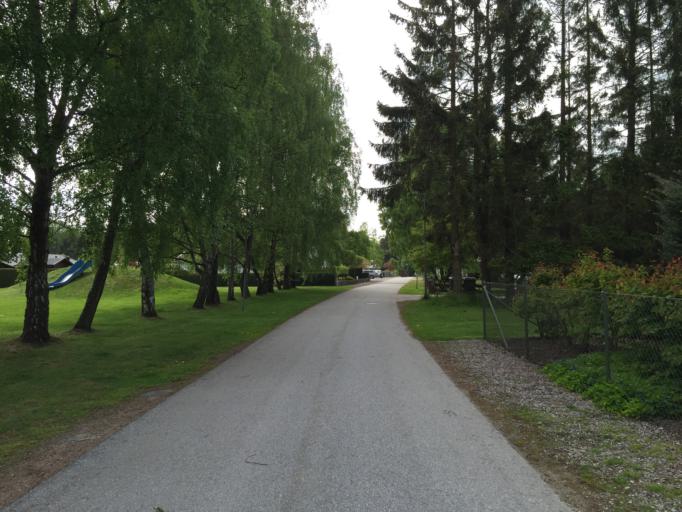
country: SE
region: Skane
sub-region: Lunds Kommun
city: Veberod
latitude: 55.6328
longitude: 13.5078
